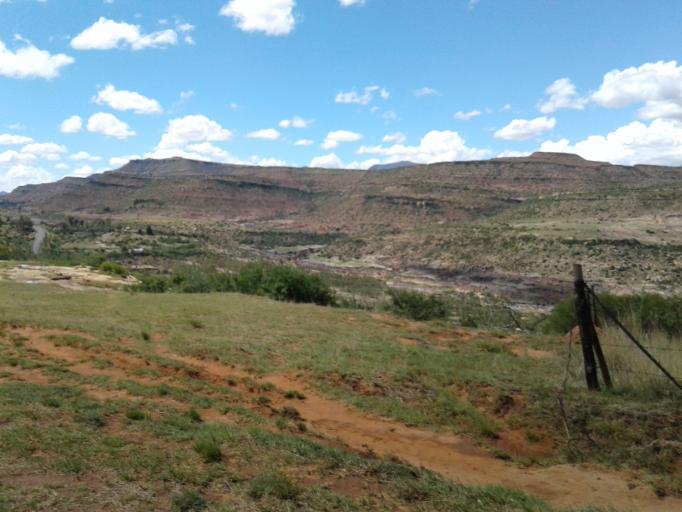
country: LS
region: Quthing
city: Quthing
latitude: -30.3728
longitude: 27.5531
